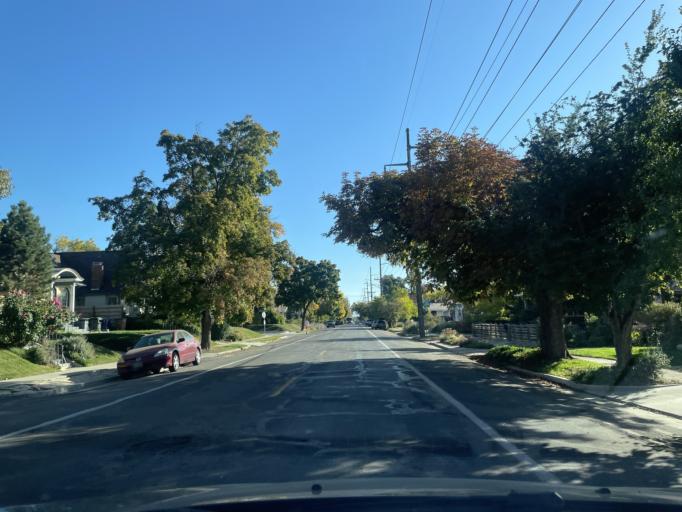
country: US
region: Utah
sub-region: Salt Lake County
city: Salt Lake City
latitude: 40.7483
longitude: -111.8596
